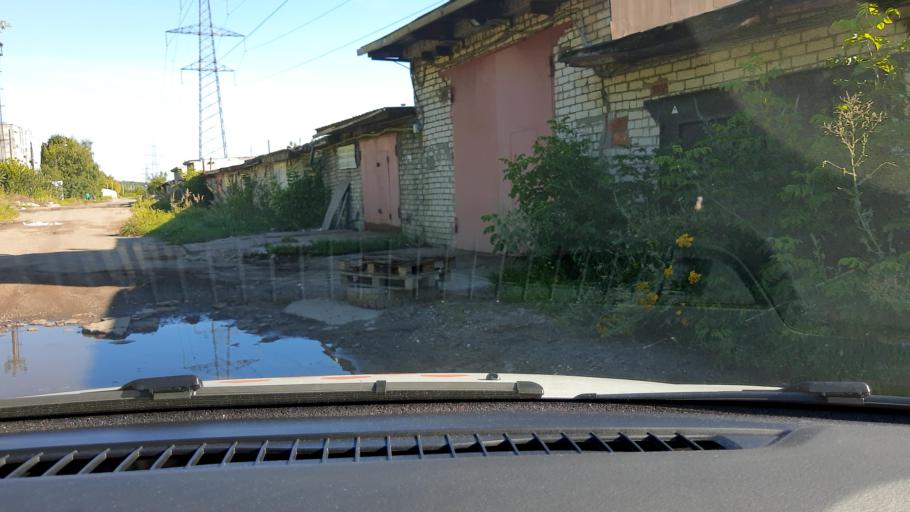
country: RU
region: Nizjnij Novgorod
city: Nizhniy Novgorod
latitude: 56.2737
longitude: 43.8969
